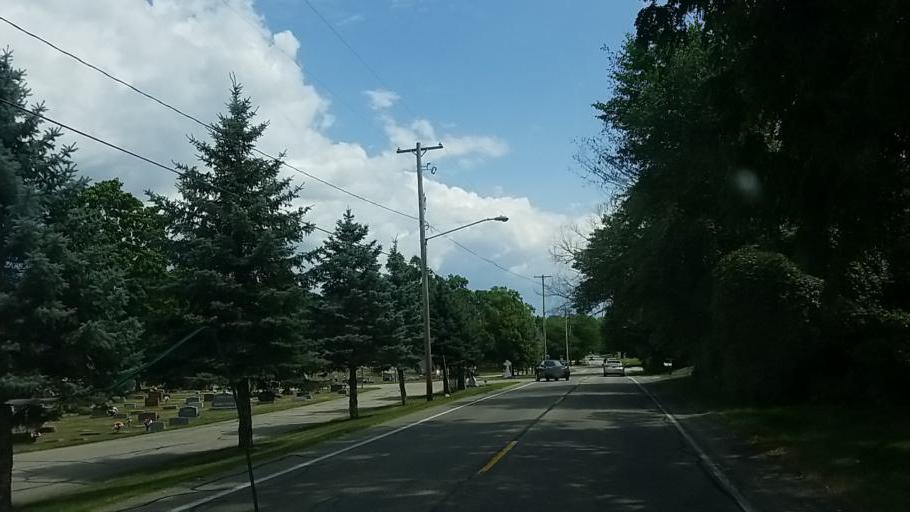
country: US
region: Michigan
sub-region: Kent County
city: Walker
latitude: 42.9942
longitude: -85.7173
